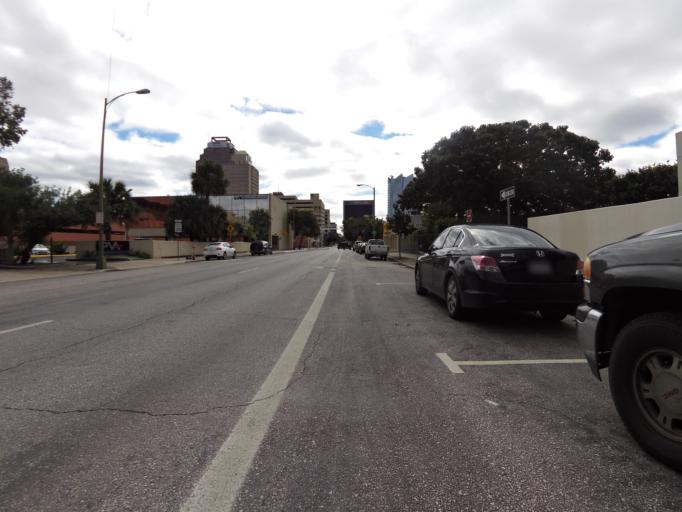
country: US
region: Texas
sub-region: Bexar County
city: San Antonio
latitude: 29.4322
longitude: -98.4940
